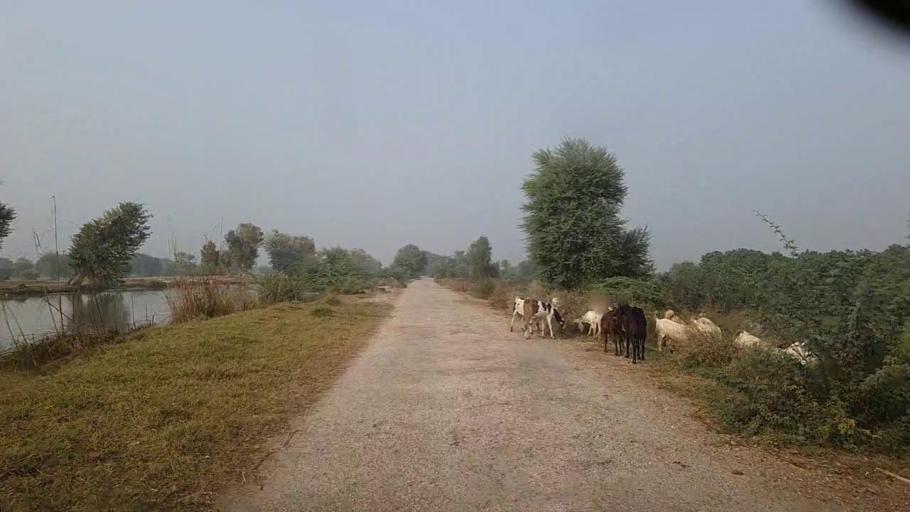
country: PK
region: Sindh
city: Bozdar
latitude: 27.1554
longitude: 68.6605
